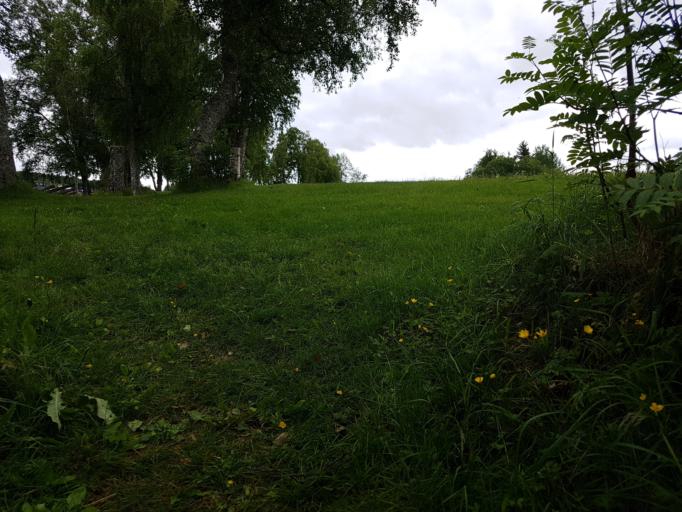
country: NO
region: Sor-Trondelag
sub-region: Selbu
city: Mebonden
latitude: 63.2352
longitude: 11.0280
